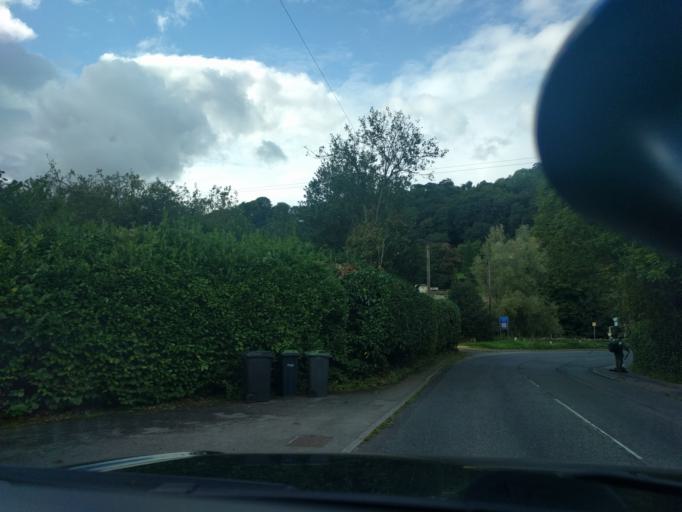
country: GB
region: England
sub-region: Bath and North East Somerset
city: Freshford
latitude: 51.3498
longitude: -2.3126
